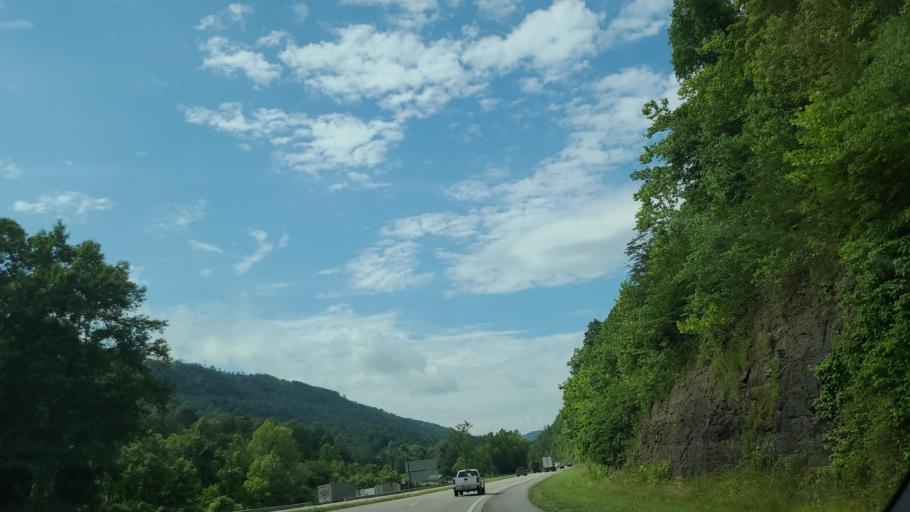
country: US
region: Kentucky
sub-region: Bell County
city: Pineville
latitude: 36.6941
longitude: -83.6848
